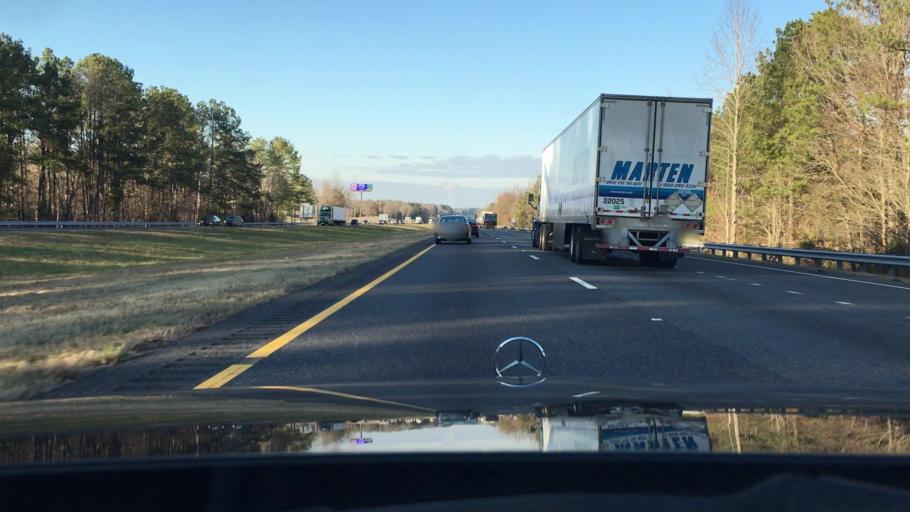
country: US
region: South Carolina
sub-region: York County
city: Lesslie
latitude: 34.7510
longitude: -81.0358
